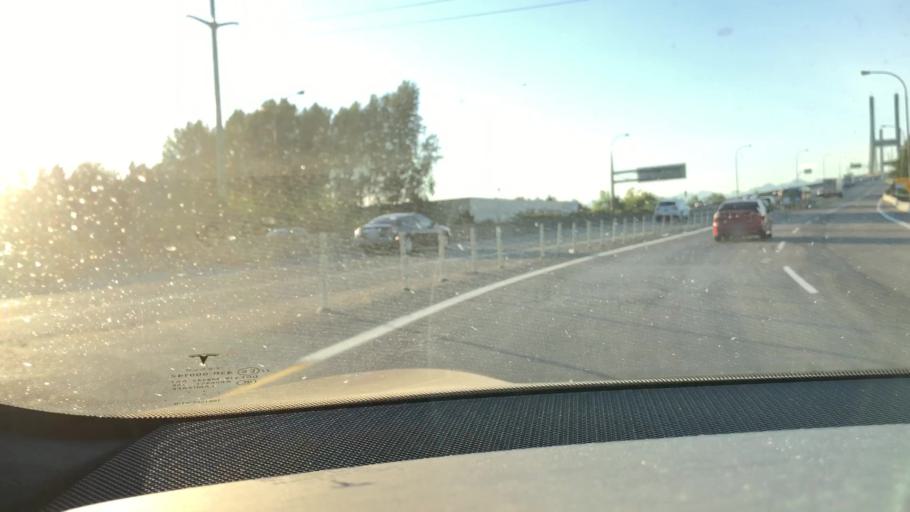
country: CA
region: British Columbia
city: Delta
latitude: 49.1473
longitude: -122.9373
